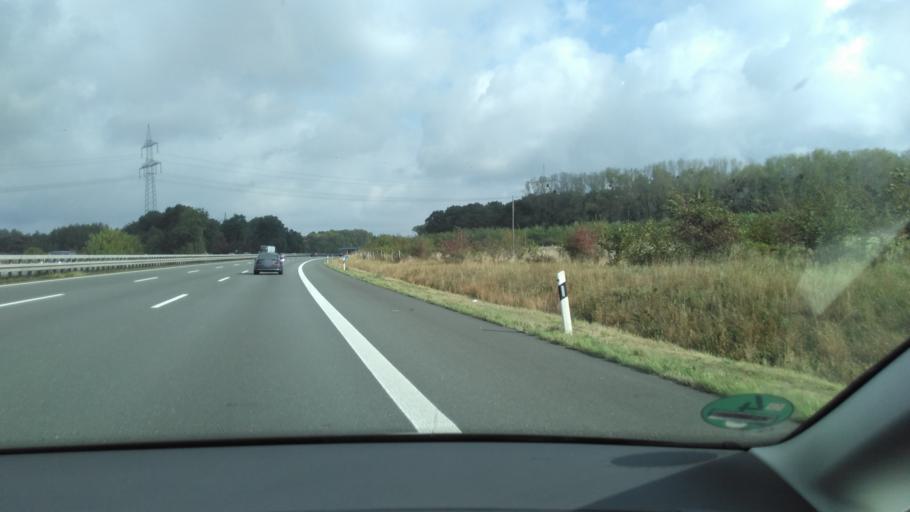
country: DE
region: North Rhine-Westphalia
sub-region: Regierungsbezirk Arnsberg
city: Welver
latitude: 51.6680
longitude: 7.9326
